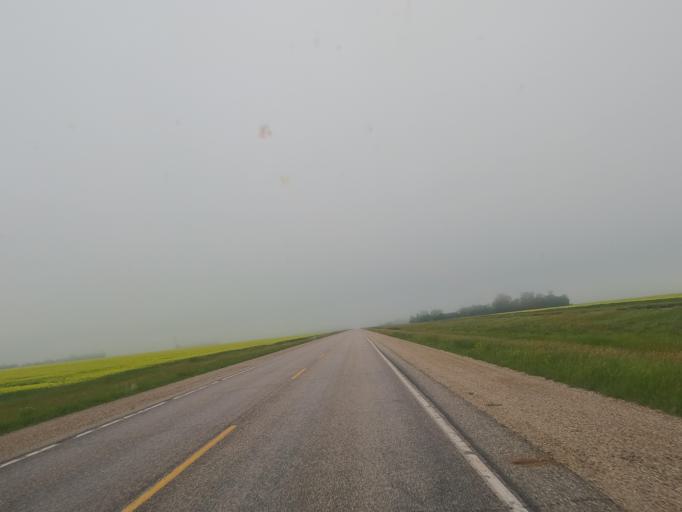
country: CA
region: Manitoba
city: Carman
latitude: 49.7196
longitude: -97.8927
